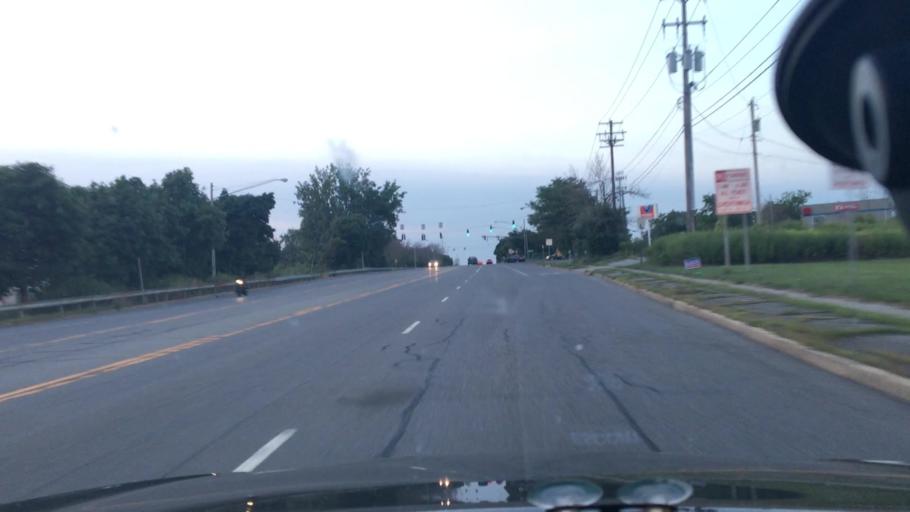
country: US
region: New York
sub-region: Erie County
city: Cheektowaga
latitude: 42.8647
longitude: -78.7543
